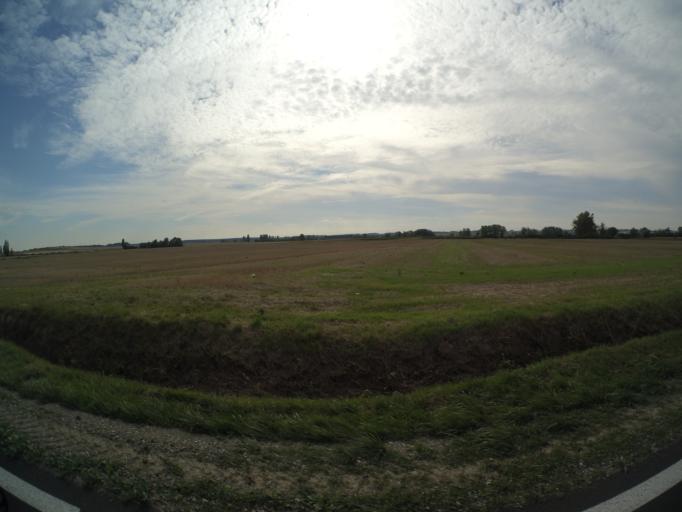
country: FR
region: Pays de la Loire
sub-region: Departement de Maine-et-Loire
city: Doue-la-Fontaine
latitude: 47.1988
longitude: -0.2317
